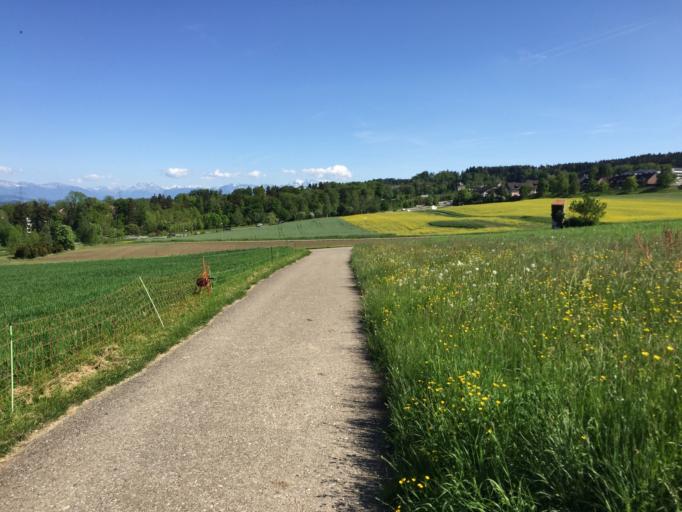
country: CH
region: Zurich
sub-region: Bezirk Uster
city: Pfaffhausen
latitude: 47.3634
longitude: 8.6268
